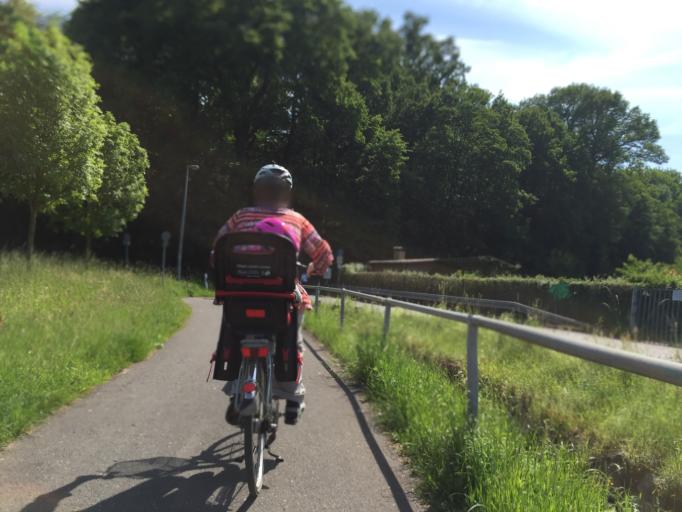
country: DE
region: Bavaria
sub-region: Regierungsbezirk Unterfranken
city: Goldbach
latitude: 49.9863
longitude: 9.1731
